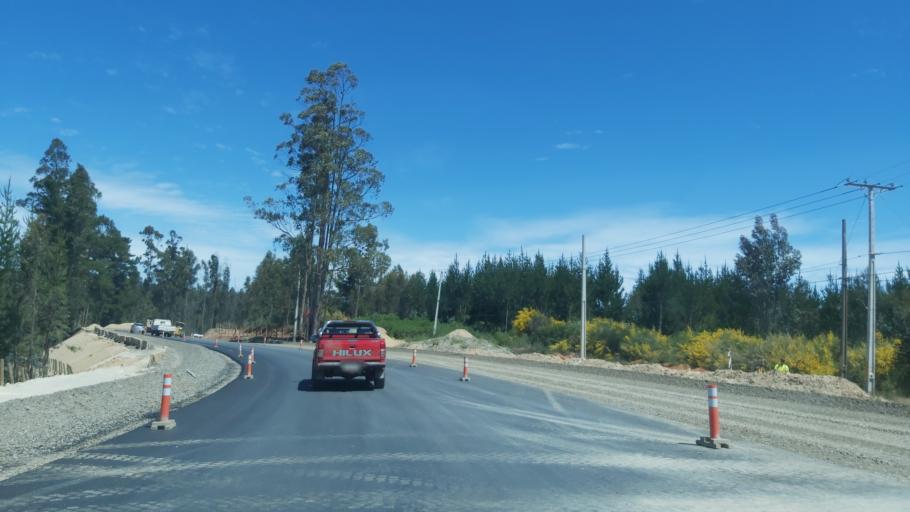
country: CL
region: Maule
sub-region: Provincia de Talca
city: Constitucion
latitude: -35.3832
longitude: -72.4209
